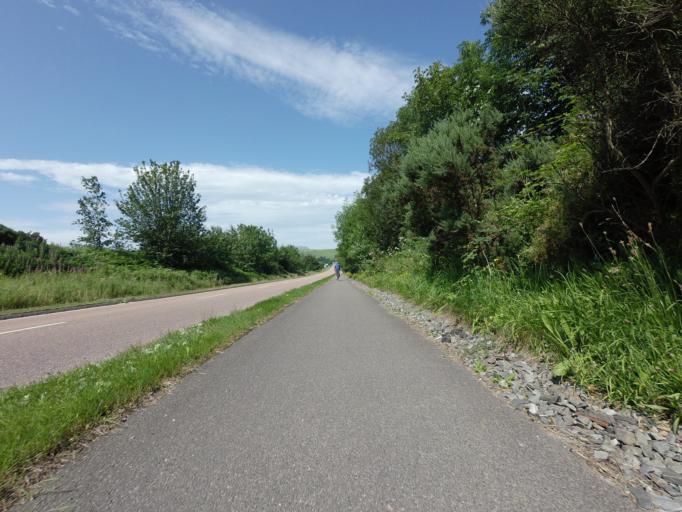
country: GB
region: Scotland
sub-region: Highland
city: Conon Bridge
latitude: 57.5702
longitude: -4.4273
